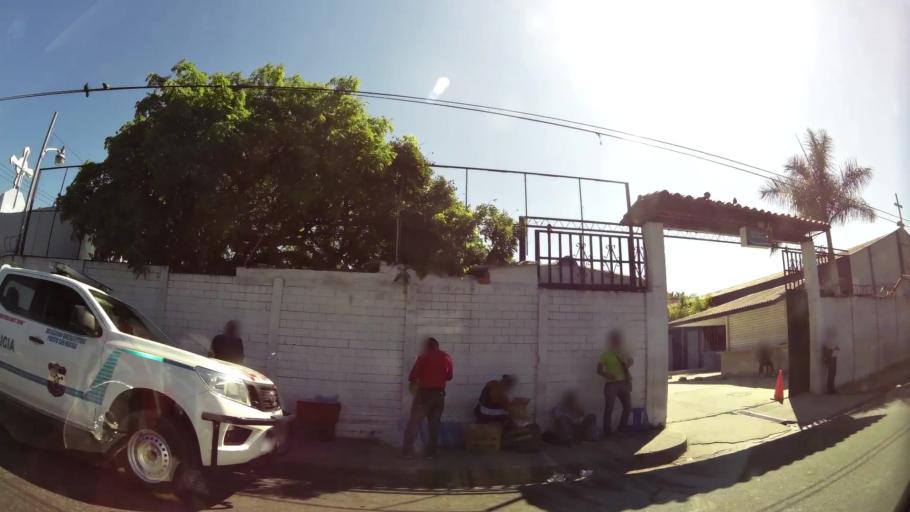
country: SV
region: La Libertad
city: Santa Tecla
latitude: 13.6717
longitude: -89.2847
